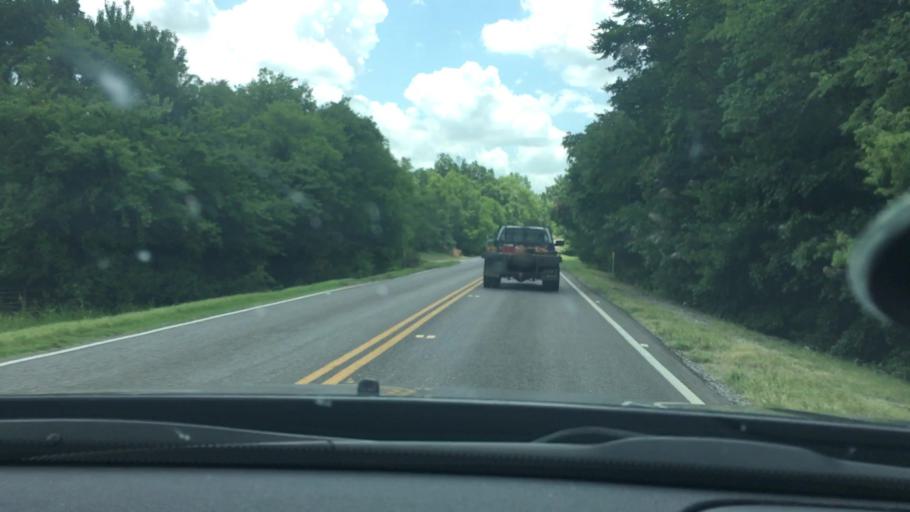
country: US
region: Oklahoma
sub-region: Pontotoc County
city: Ada
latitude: 34.5750
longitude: -96.6302
